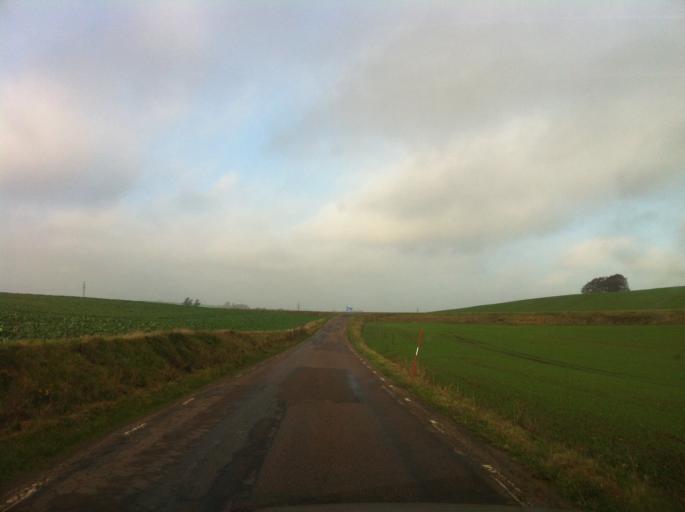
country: SE
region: Skane
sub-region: Landskrona
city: Asmundtorp
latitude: 55.9041
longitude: 12.9232
